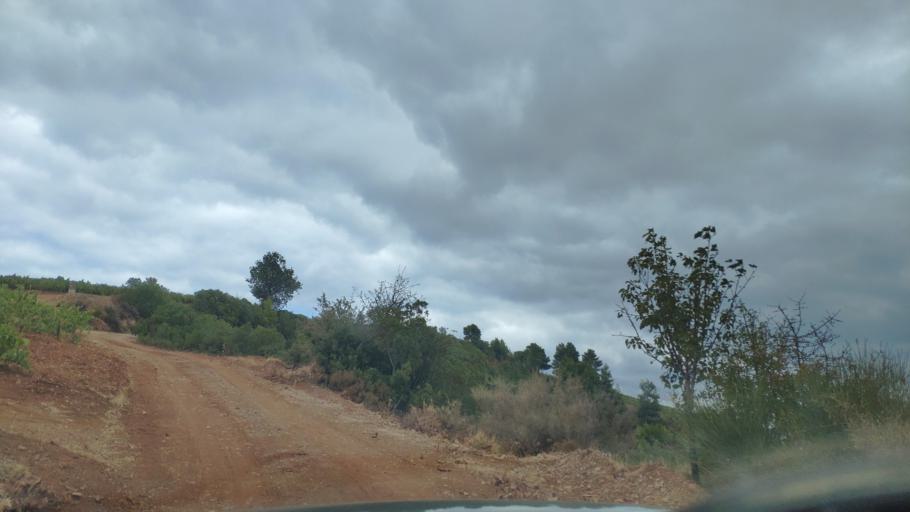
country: GR
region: West Greece
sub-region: Nomos Achaias
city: Temeni
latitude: 38.1778
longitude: 22.1597
